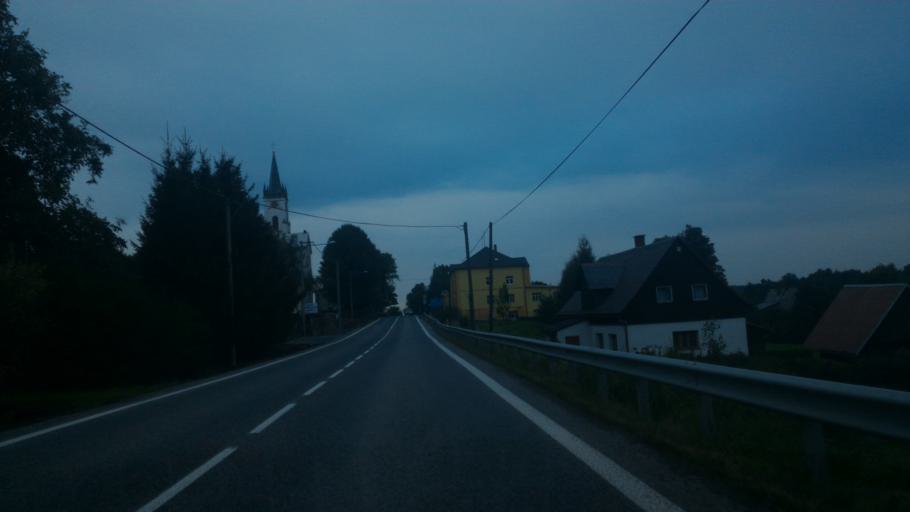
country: CZ
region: Ustecky
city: Dolni Podluzi
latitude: 50.9071
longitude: 14.5676
